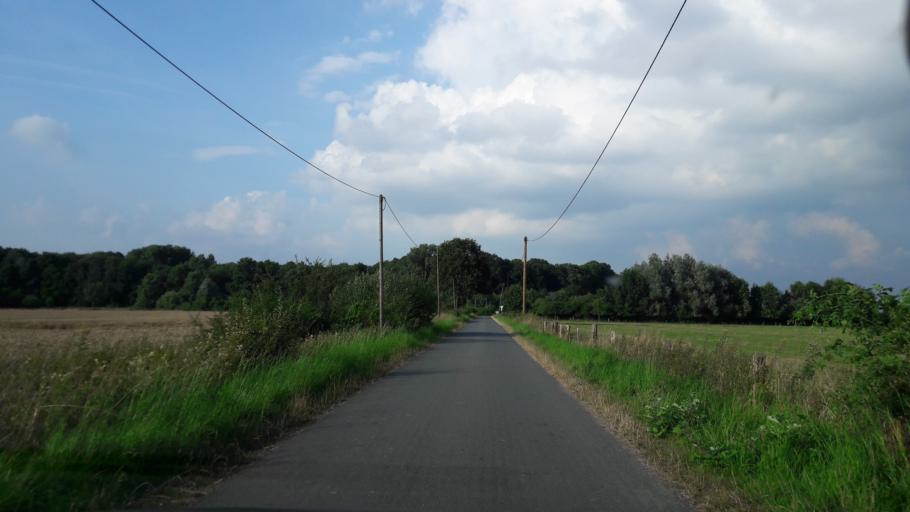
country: DE
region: North Rhine-Westphalia
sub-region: Regierungsbezirk Munster
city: Everswinkel
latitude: 51.9008
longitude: 7.7800
